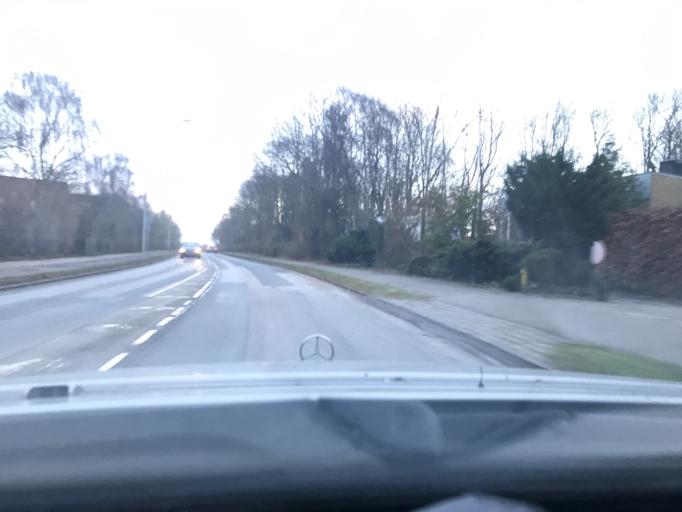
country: DK
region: South Denmark
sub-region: Sonderborg Kommune
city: Nordborg
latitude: 55.0542
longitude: 9.7504
